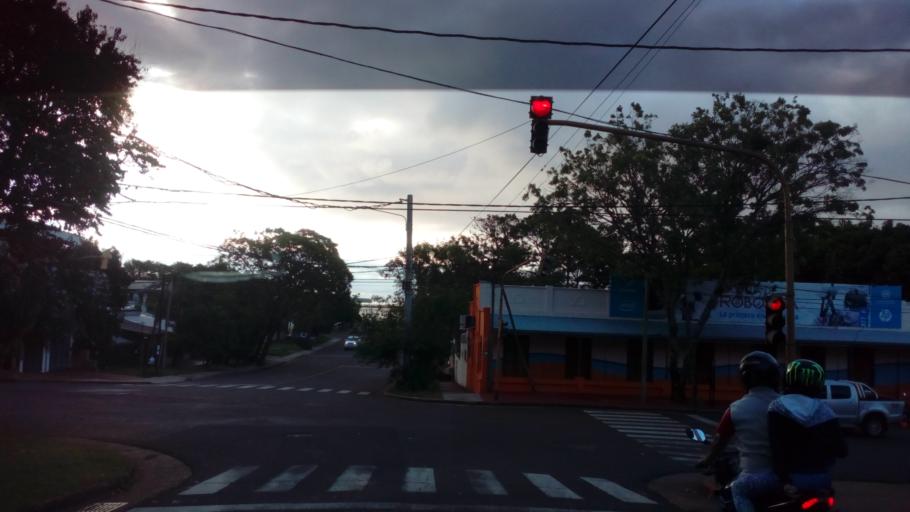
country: AR
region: Misiones
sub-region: Departamento de Capital
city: Posadas
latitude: -27.3532
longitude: -55.8993
